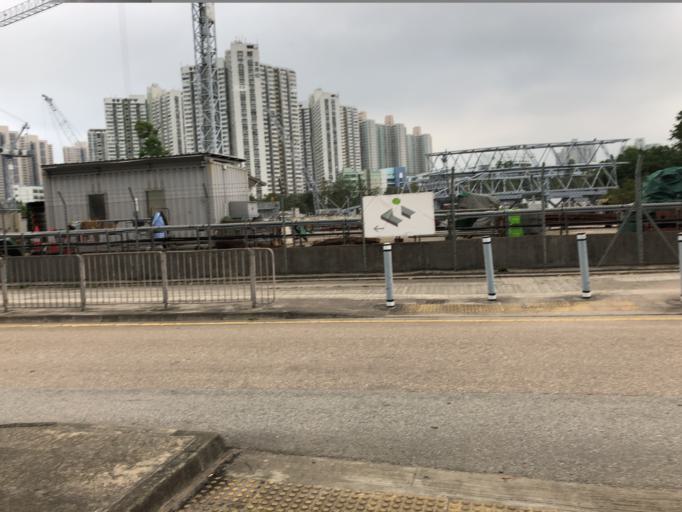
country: HK
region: Tai Po
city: Tai Po
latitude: 22.4561
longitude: 114.1799
